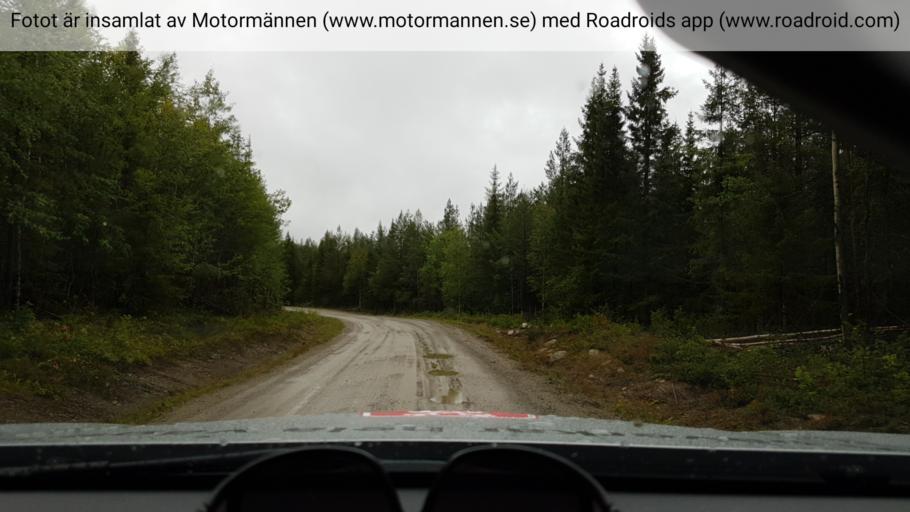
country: SE
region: Vaesterbotten
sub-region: Storumans Kommun
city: Storuman
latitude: 64.9097
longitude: 17.4752
